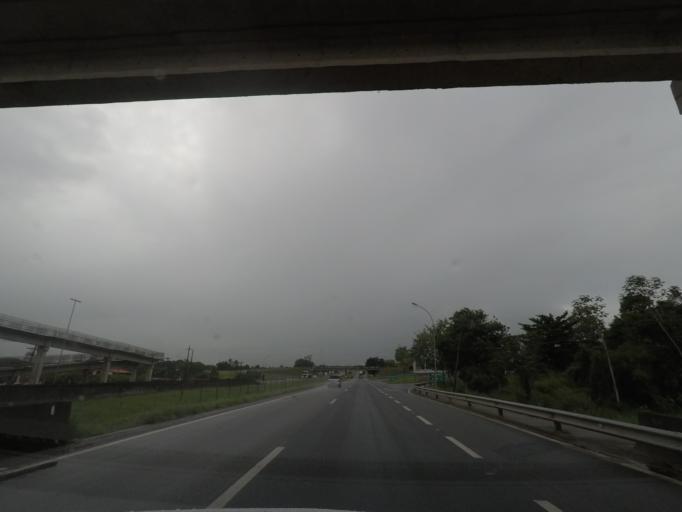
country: BR
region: Sao Paulo
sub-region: Registro
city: Registro
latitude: -24.4603
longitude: -47.8162
